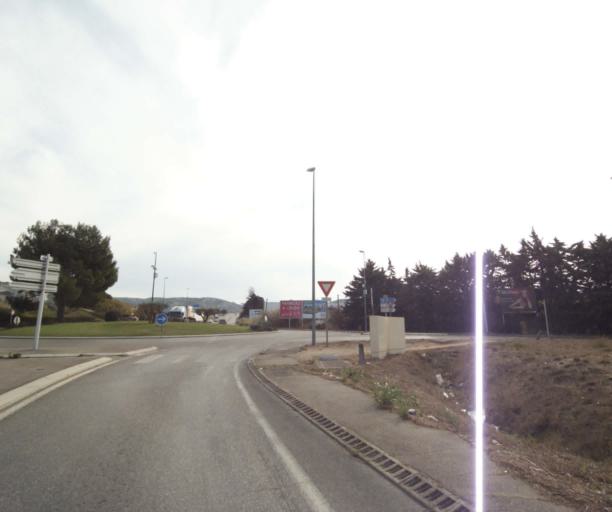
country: FR
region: Provence-Alpes-Cote d'Azur
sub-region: Departement des Bouches-du-Rhone
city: Gignac-la-Nerthe
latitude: 43.3854
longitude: 5.2179
